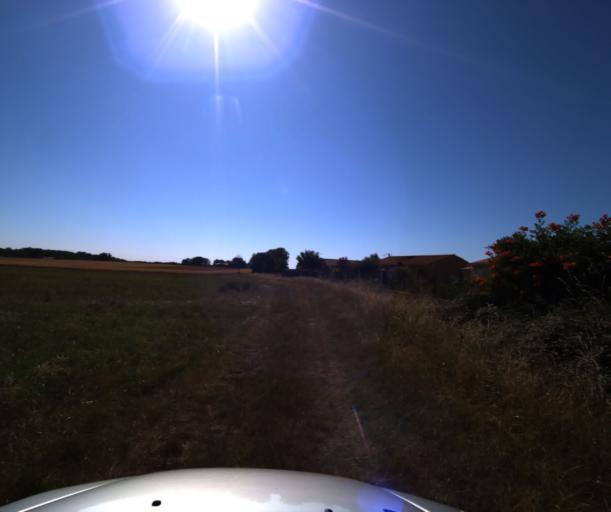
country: FR
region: Midi-Pyrenees
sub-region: Departement de la Haute-Garonne
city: Eaunes
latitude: 43.4207
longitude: 1.3573
